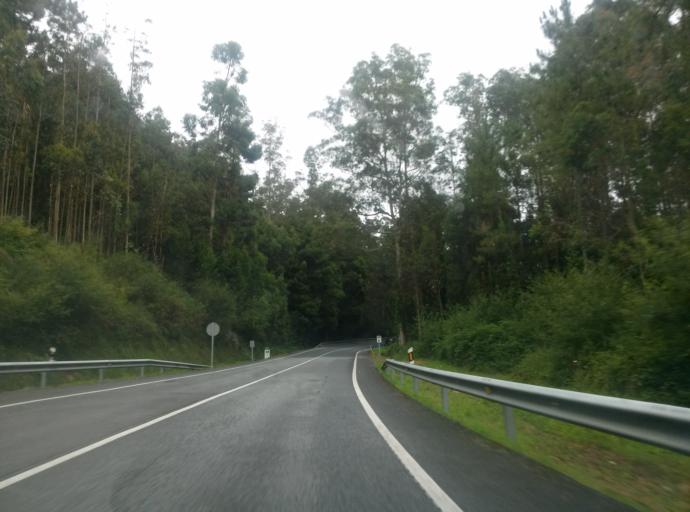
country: ES
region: Galicia
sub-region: Provincia de Lugo
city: Viveiro
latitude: 43.6063
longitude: -7.6083
